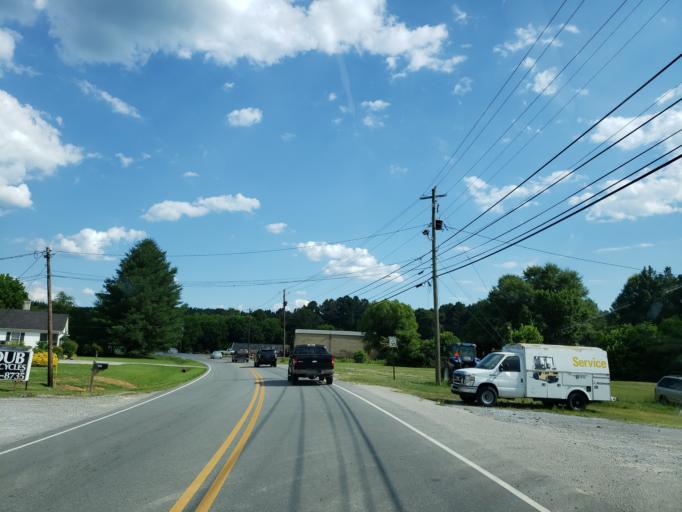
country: US
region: Georgia
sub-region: Polk County
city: Rockmart
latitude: 33.9867
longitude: -85.0416
